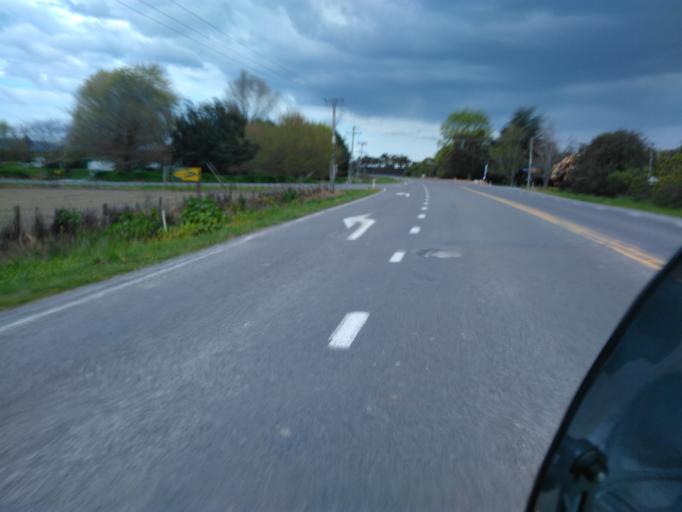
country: NZ
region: Gisborne
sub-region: Gisborne District
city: Gisborne
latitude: -38.6563
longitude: 177.9238
